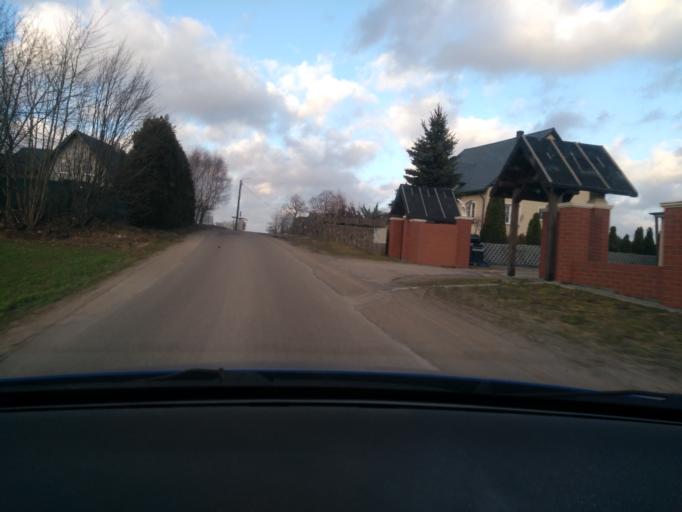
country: PL
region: Pomeranian Voivodeship
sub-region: Powiat kartuski
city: Przodkowo
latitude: 54.4052
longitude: 18.2312
